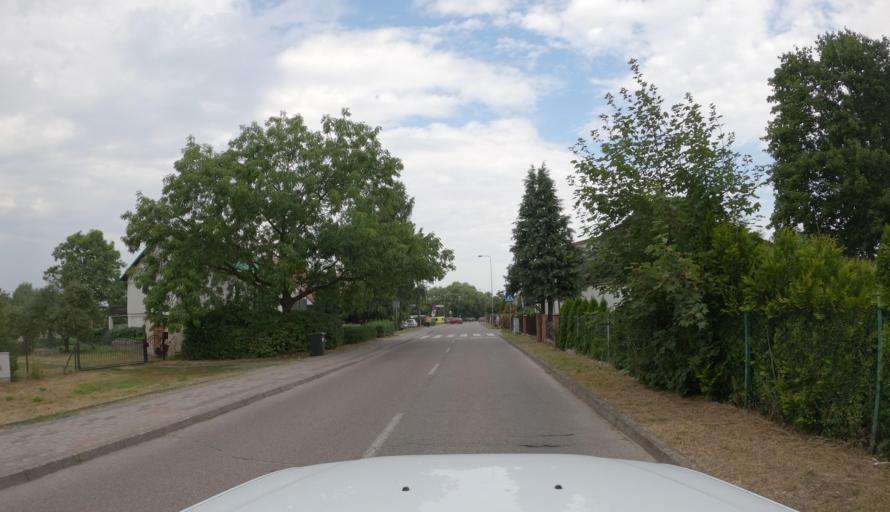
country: PL
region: West Pomeranian Voivodeship
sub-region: Powiat bialogardzki
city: Bialogard
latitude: 54.0092
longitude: 15.9958
